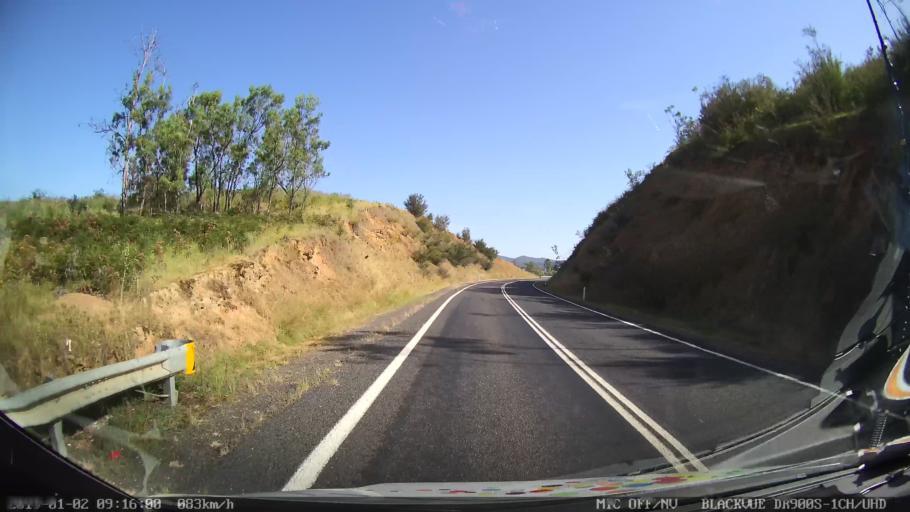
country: AU
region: New South Wales
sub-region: Tumut Shire
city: Tumut
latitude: -35.4582
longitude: 148.2818
